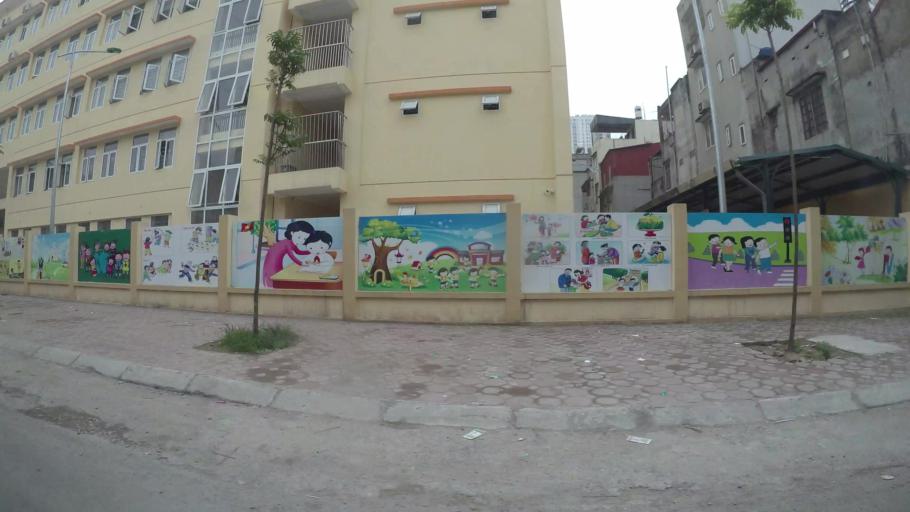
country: VN
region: Ha Noi
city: Ha Dong
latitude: 20.9692
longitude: 105.7707
